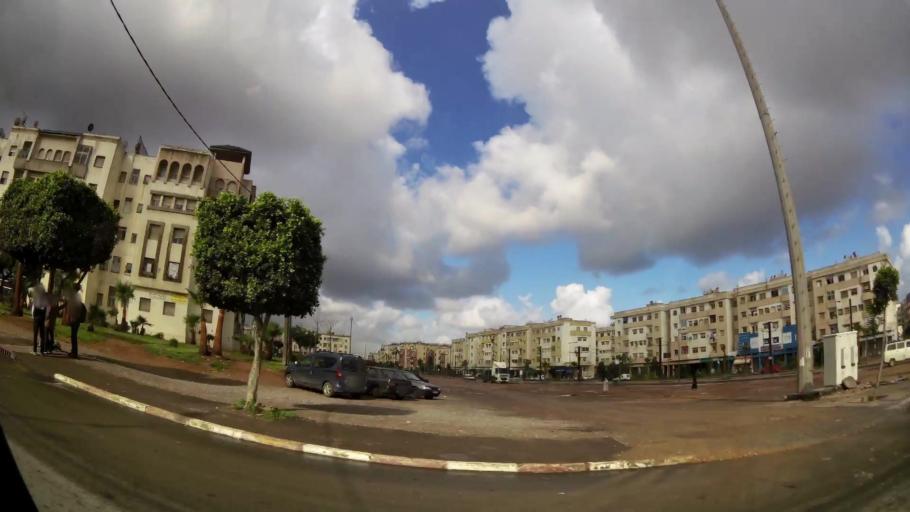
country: MA
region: Grand Casablanca
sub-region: Mediouna
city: Tit Mellil
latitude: 33.5993
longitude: -7.5310
